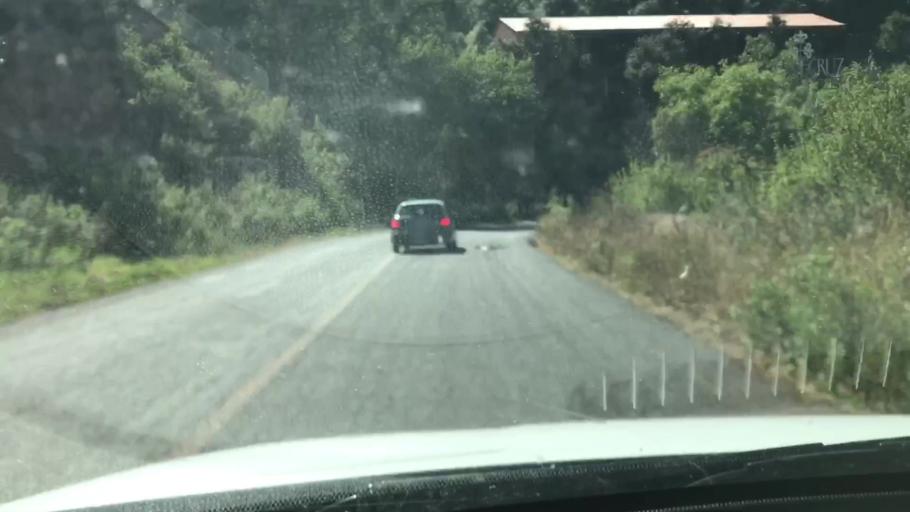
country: MX
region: Jalisco
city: Chiquilistlan
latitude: 20.1408
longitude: -103.7192
